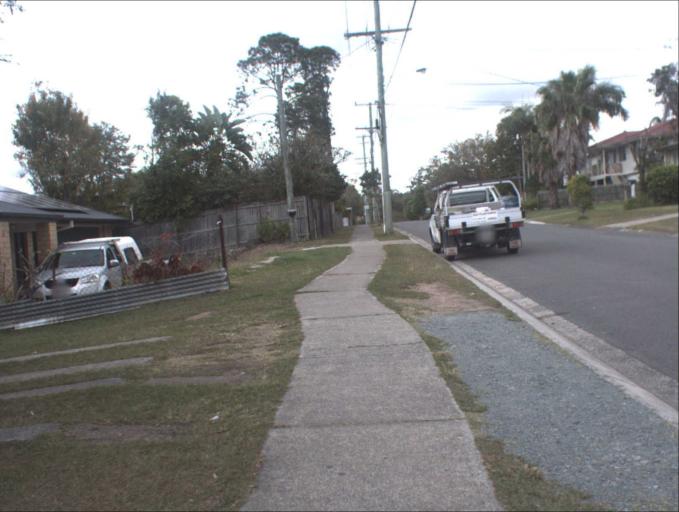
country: AU
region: Queensland
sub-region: Logan
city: Logan City
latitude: -27.6331
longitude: 153.1067
